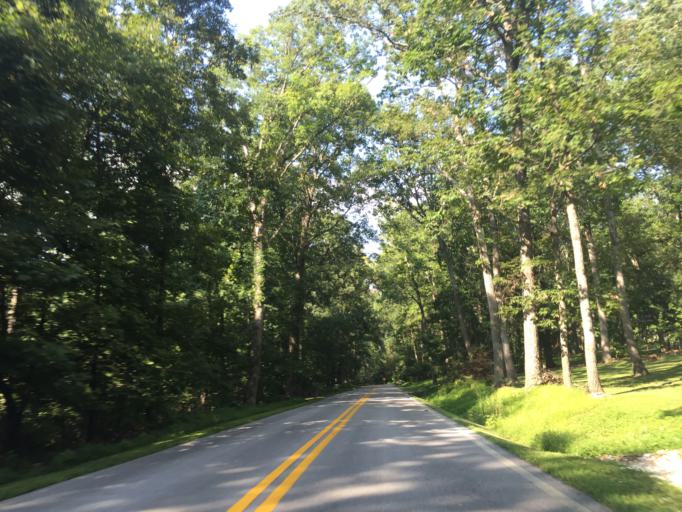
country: US
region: Maryland
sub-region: Carroll County
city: Manchester
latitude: 39.6380
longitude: -76.9173
